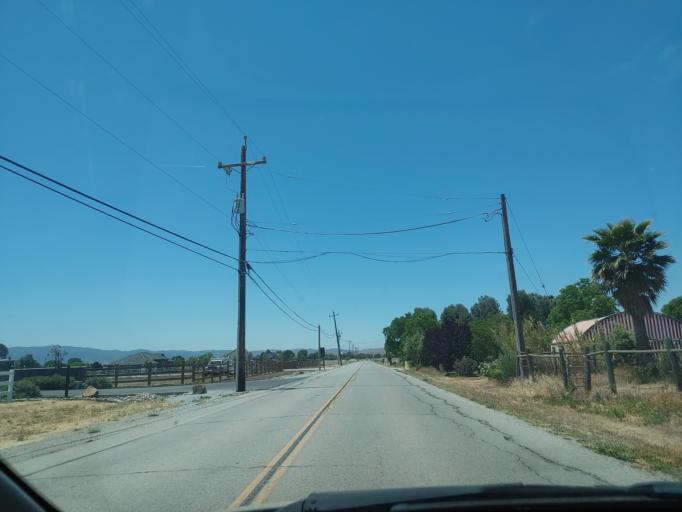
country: US
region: California
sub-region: San Benito County
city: Hollister
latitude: 36.9137
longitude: -121.3608
